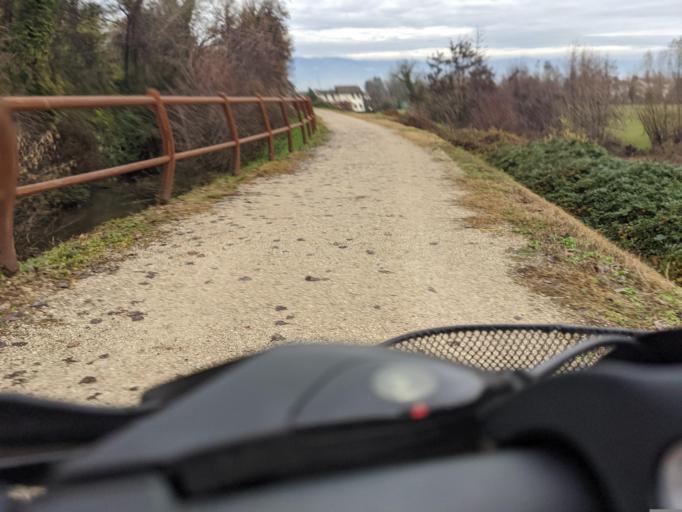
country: IT
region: Veneto
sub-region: Provincia di Vicenza
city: Dueville
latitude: 45.6209
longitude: 11.5331
